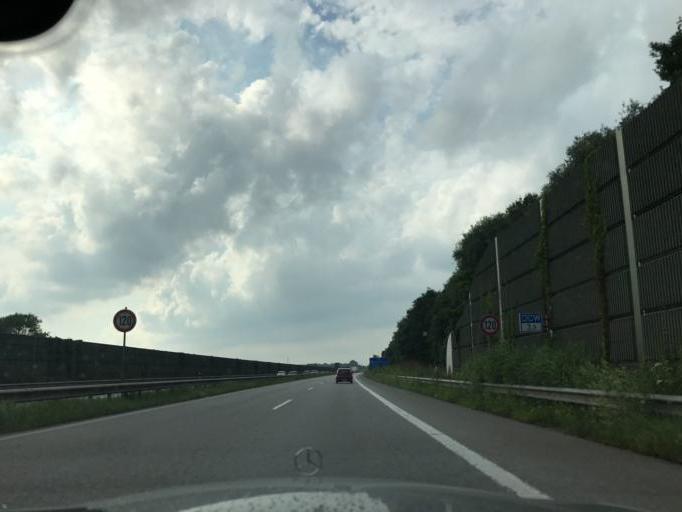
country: DE
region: Hamburg
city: Wandsbek
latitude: 53.4891
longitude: 10.1093
